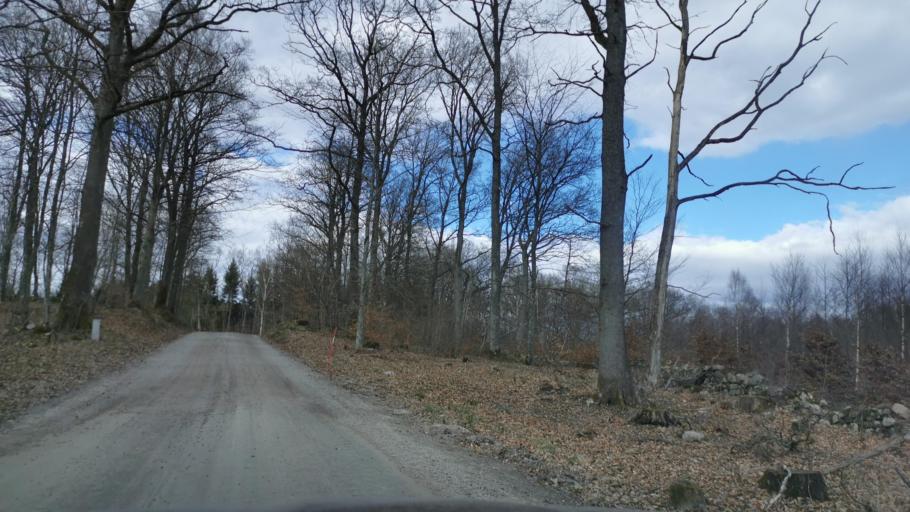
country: SE
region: Skane
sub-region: Sjobo Kommun
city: Sjoebo
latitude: 55.7446
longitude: 13.8382
